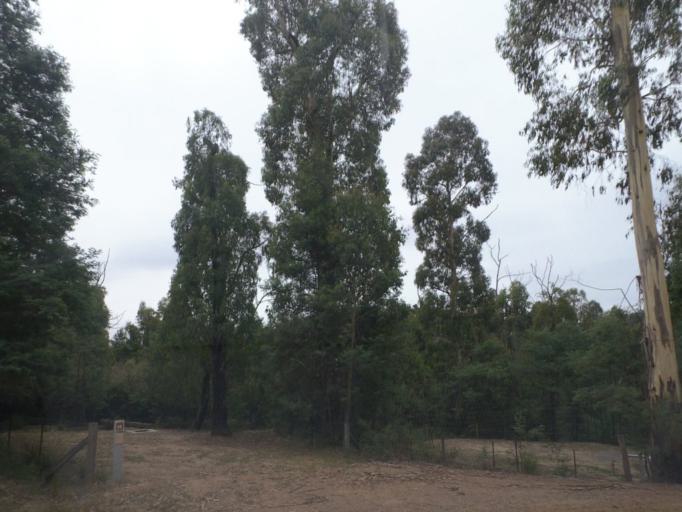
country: AU
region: Victoria
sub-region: Yarra Ranges
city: Healesville
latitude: -37.4257
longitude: 145.5687
